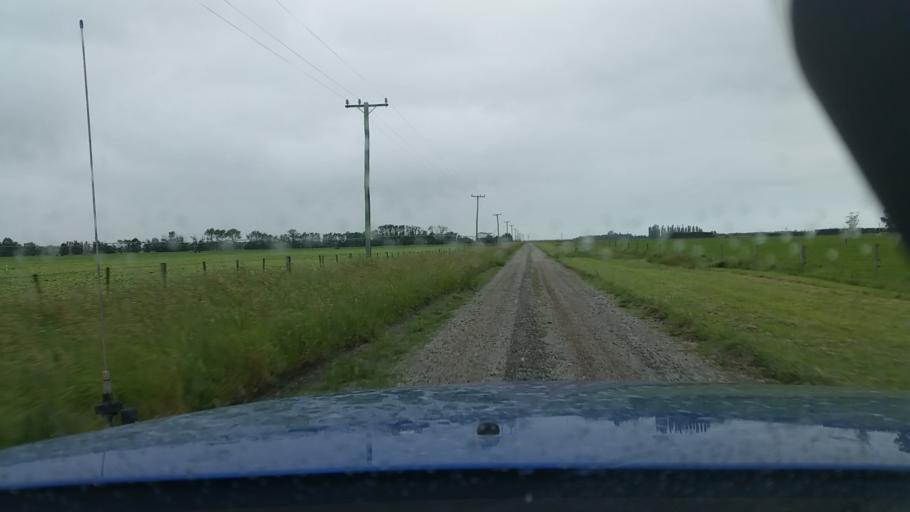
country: NZ
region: Canterbury
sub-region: Ashburton District
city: Tinwald
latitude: -44.0466
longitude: 171.6549
